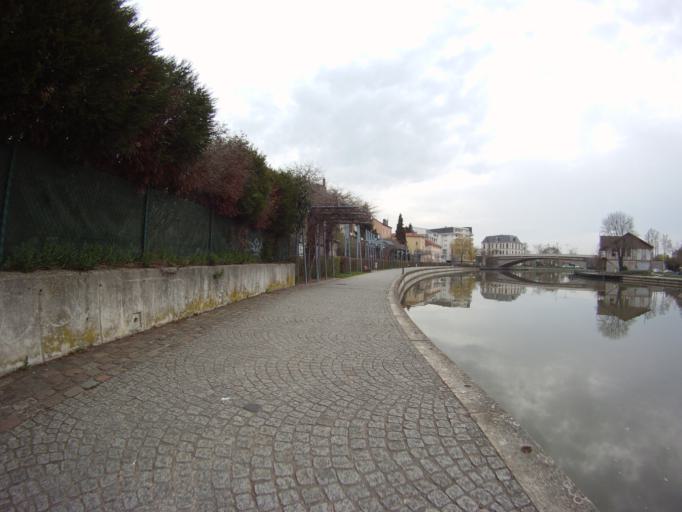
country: FR
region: Lorraine
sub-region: Departement de Meurthe-et-Moselle
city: Saint-Max
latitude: 48.7004
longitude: 6.2017
